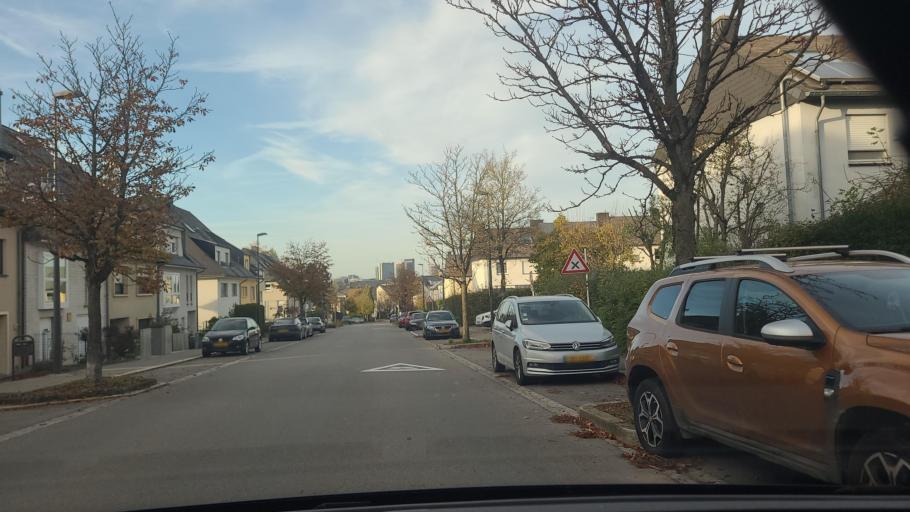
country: LU
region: Luxembourg
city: Itzig
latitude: 49.5943
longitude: 6.1507
